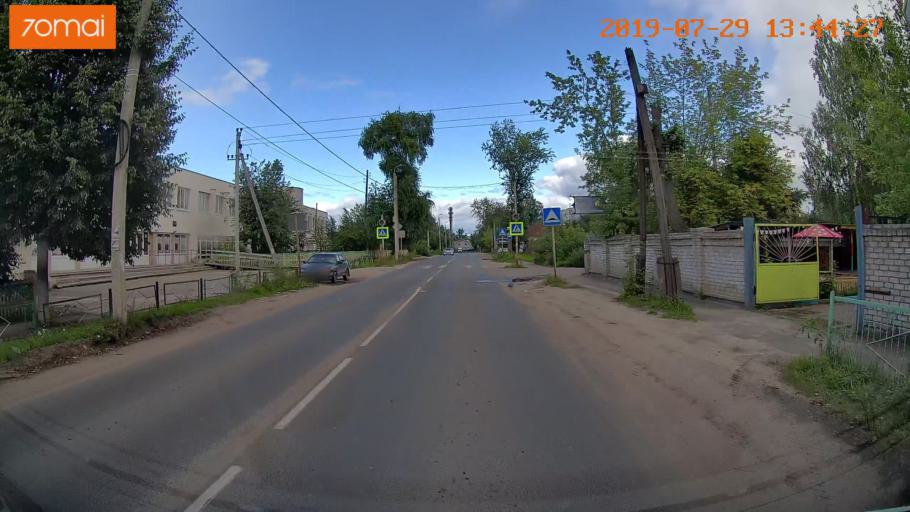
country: RU
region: Ivanovo
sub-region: Gorod Ivanovo
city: Ivanovo
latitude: 57.0100
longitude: 40.9341
